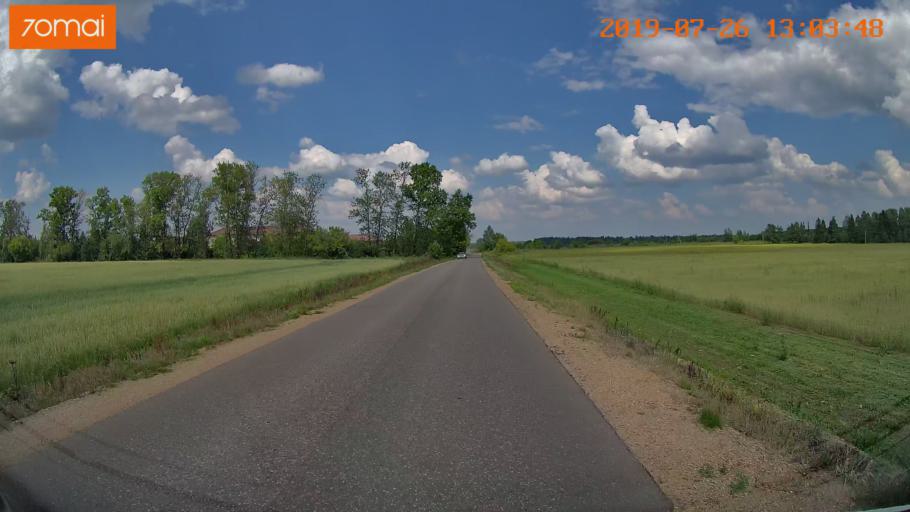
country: RU
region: Ivanovo
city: Bogorodskoye
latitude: 57.0495
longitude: 41.0220
